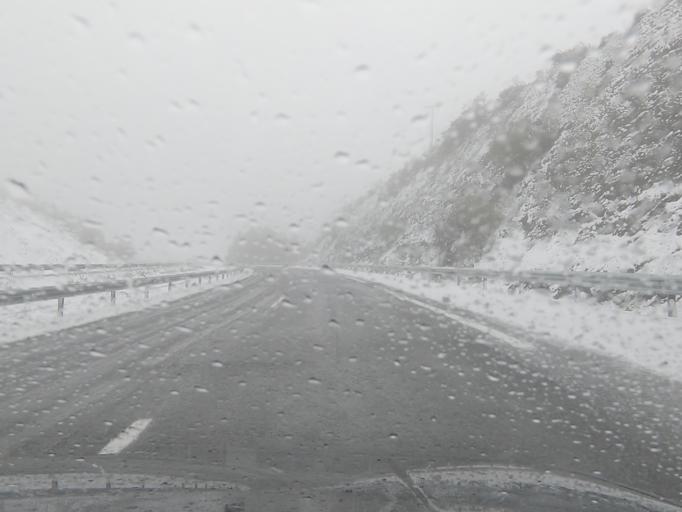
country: ES
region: Galicia
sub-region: Provincia de Ourense
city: Rios
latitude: 41.9544
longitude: -7.3268
